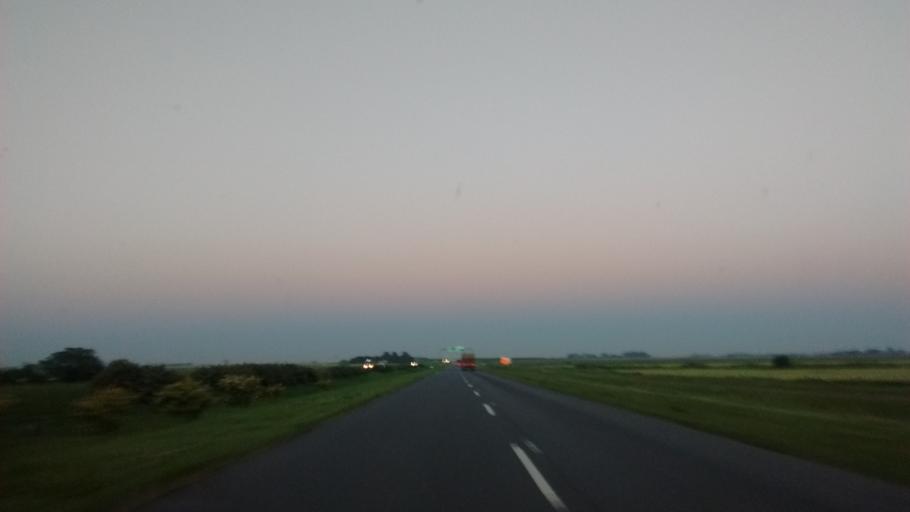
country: AR
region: Santa Fe
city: Roldan
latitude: -32.9045
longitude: -61.0110
